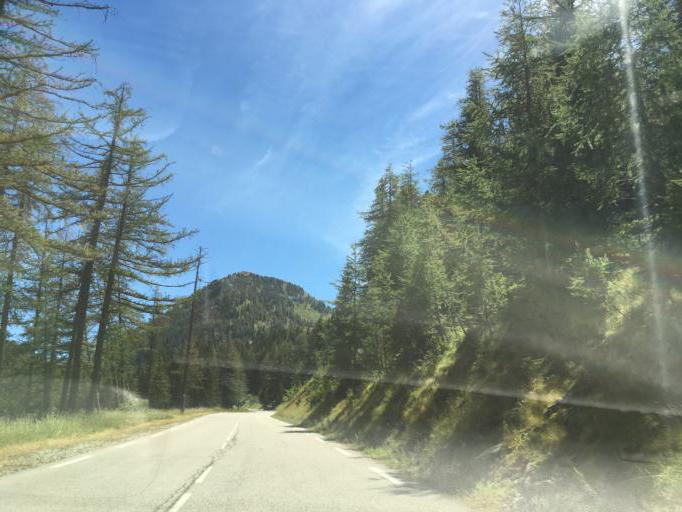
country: IT
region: Piedmont
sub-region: Provincia di Cuneo
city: Vinadio
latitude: 44.1967
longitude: 7.1268
